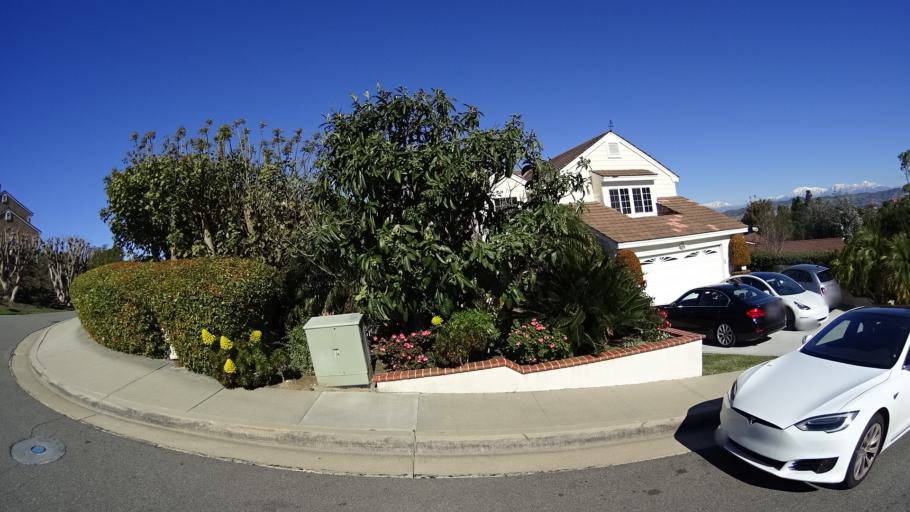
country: US
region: California
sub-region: Orange County
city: Villa Park
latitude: 33.8406
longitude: -117.8027
